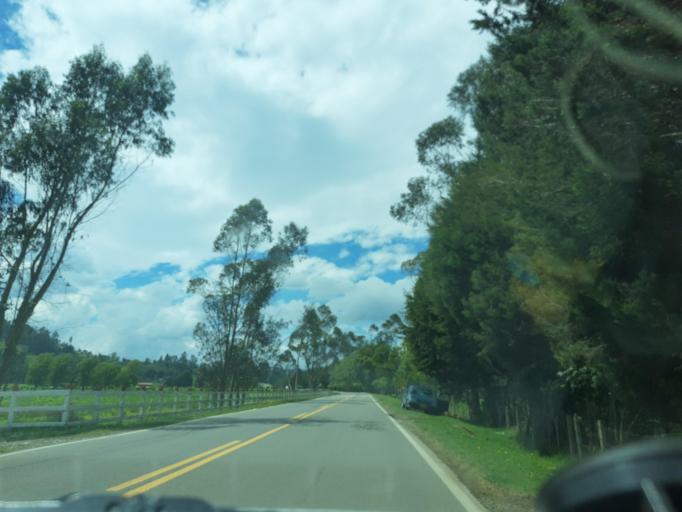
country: CO
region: Boyaca
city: Chiquinquira
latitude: 5.6235
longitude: -73.7630
